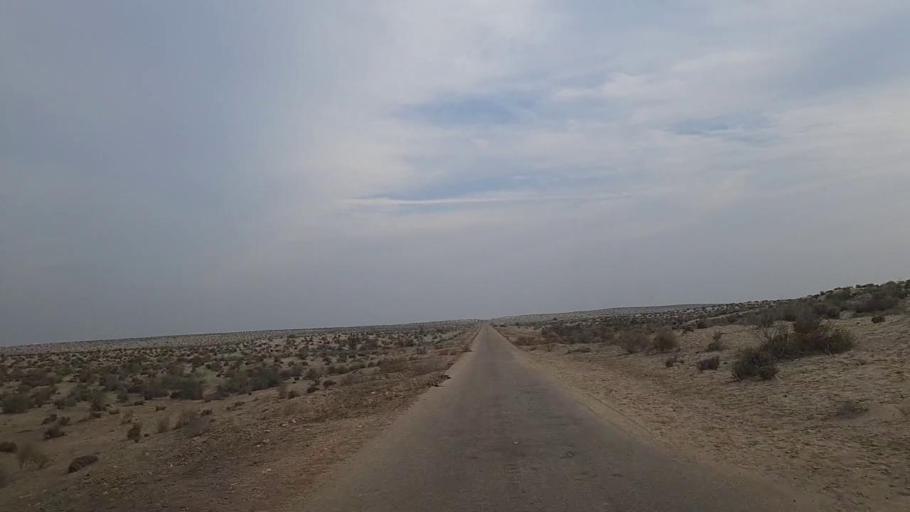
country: PK
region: Sindh
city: Daur
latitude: 26.5142
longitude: 68.5023
